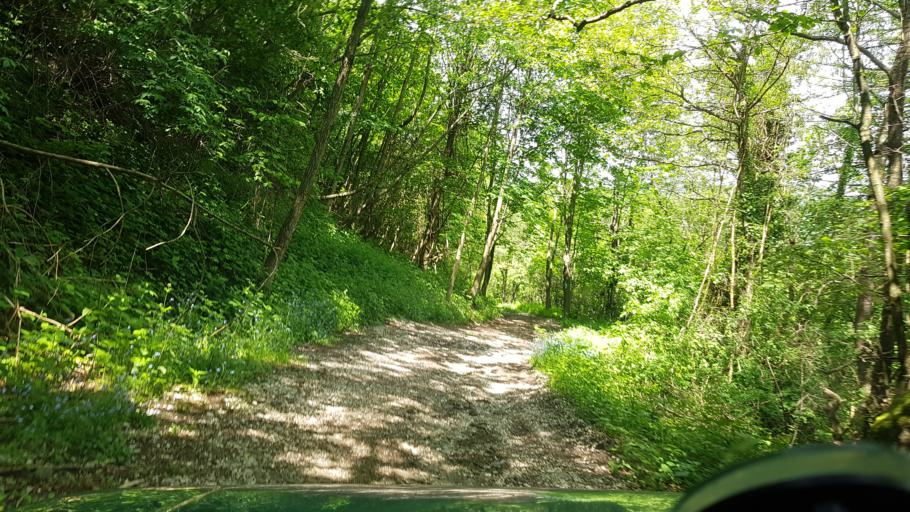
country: IT
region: Friuli Venezia Giulia
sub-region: Provincia di Udine
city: Pulfero
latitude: 46.1920
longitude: 13.4249
